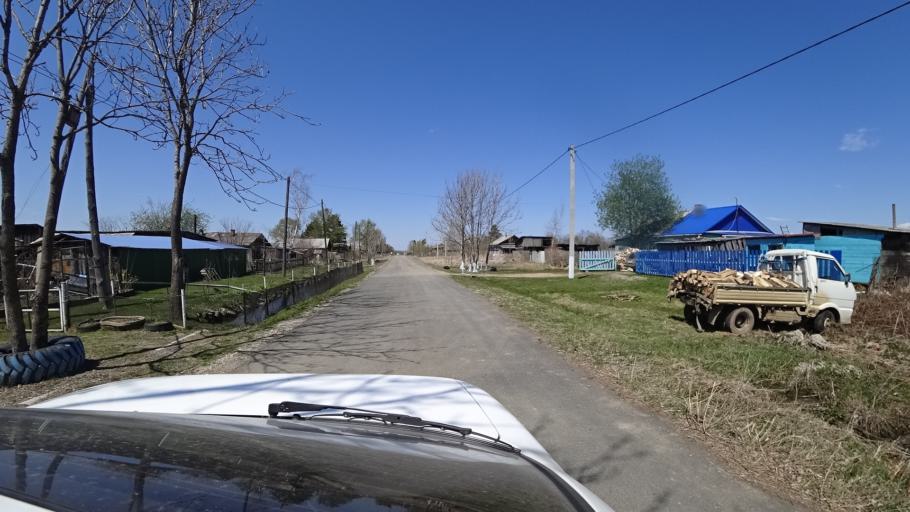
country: RU
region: Primorskiy
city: Dal'nerechensk
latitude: 45.7917
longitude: 133.7728
